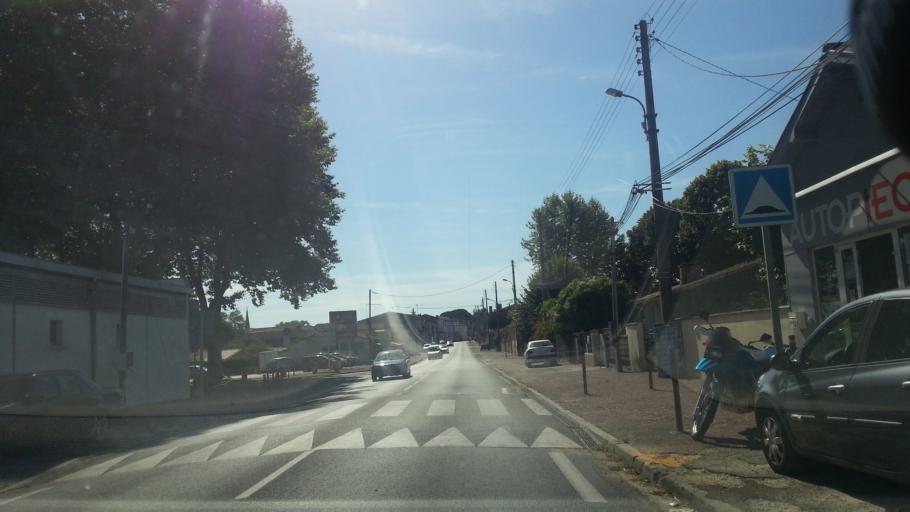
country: FR
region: Aquitaine
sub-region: Departement de la Gironde
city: Podensac
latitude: 44.6529
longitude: -0.3592
